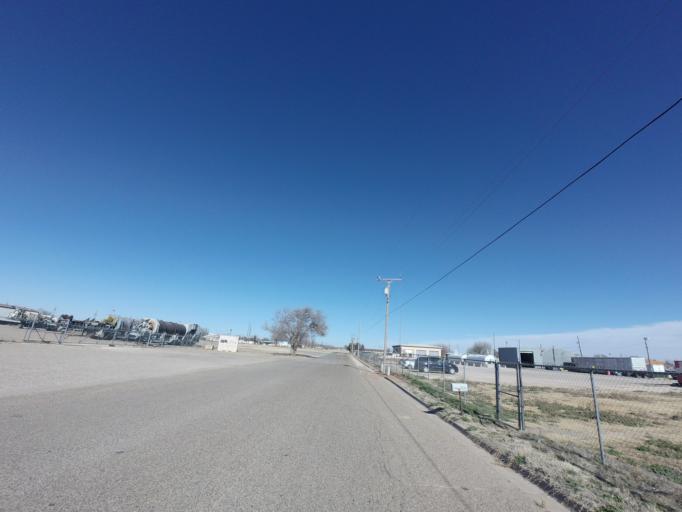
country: US
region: New Mexico
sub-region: Curry County
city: Clovis
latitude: 34.4025
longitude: -103.2366
